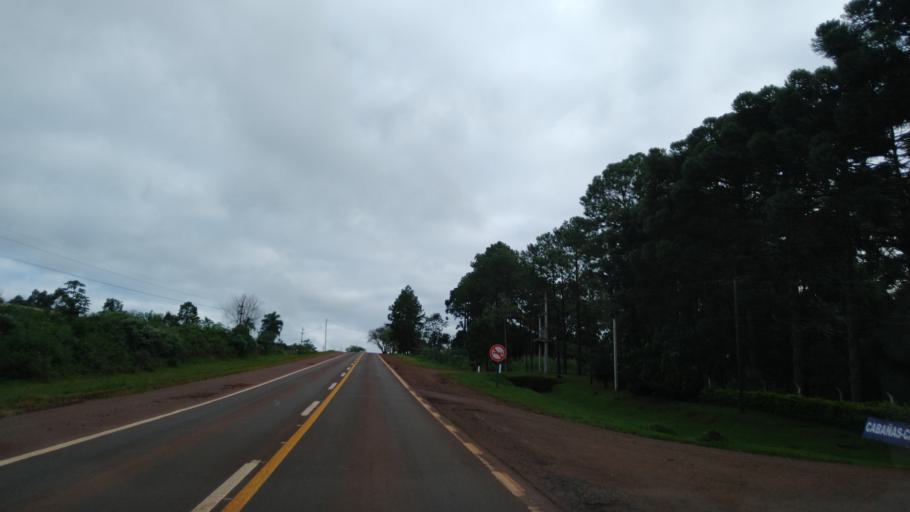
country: AR
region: Misiones
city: Jardin America
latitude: -27.0585
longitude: -55.2574
